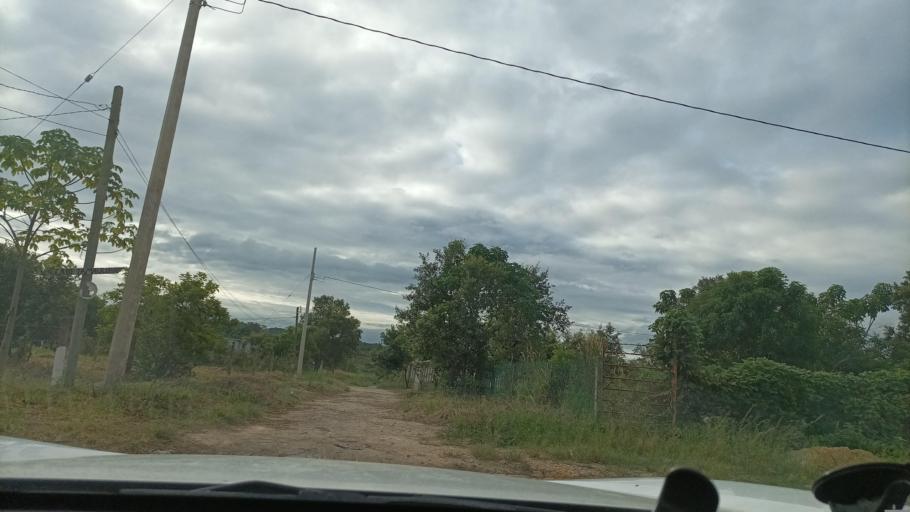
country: MX
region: Veracruz
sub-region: Cosoleacaque
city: Hermenegildo J. Aldana
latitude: 17.9951
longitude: -94.6080
